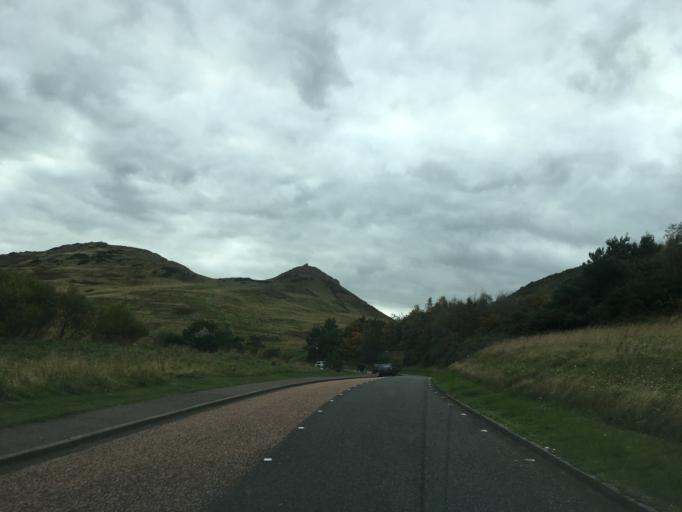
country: GB
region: Scotland
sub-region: West Lothian
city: Seafield
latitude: 55.9473
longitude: -3.1518
